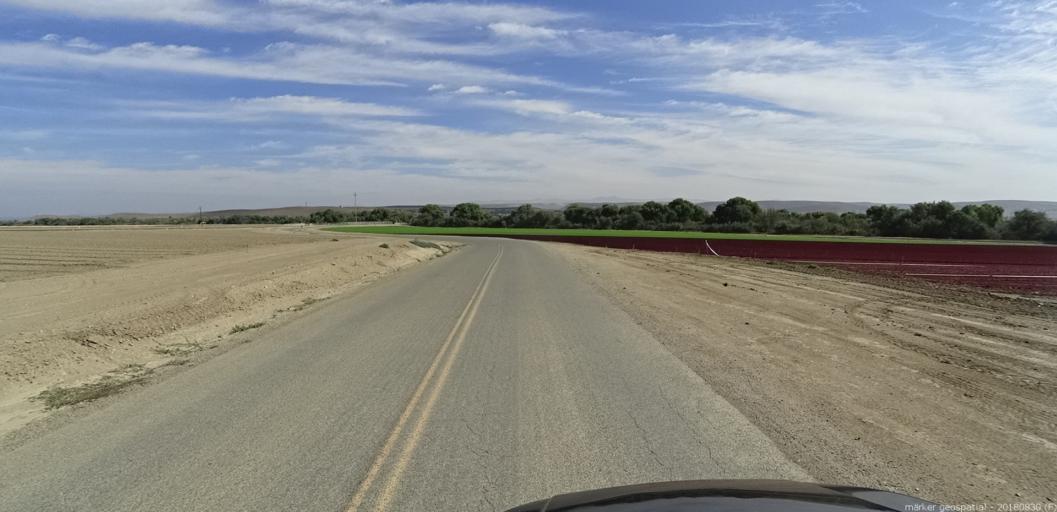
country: US
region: California
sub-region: Monterey County
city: King City
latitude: 36.1127
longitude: -121.0308
